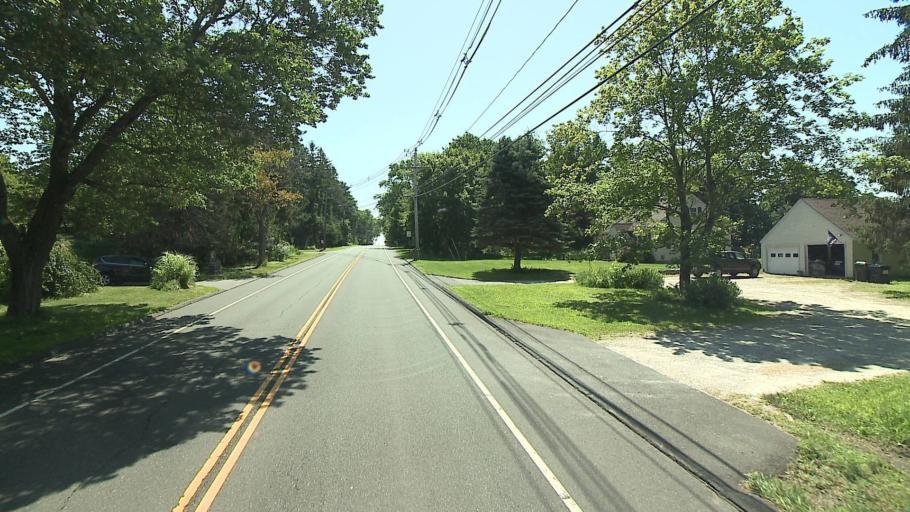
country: US
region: Connecticut
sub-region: Litchfield County
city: Litchfield
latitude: 41.8343
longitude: -73.2684
